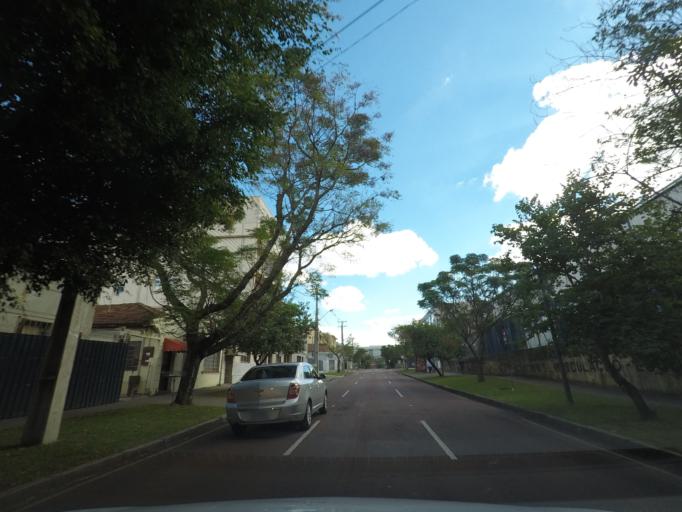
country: BR
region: Parana
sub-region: Curitiba
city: Curitiba
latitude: -25.4461
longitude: -49.2704
